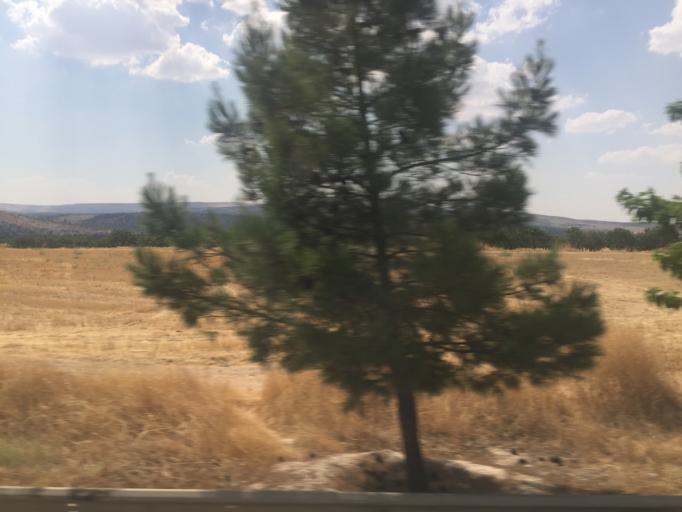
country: TR
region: Sanliurfa
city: Sanliurfa
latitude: 37.2506
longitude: 38.7930
